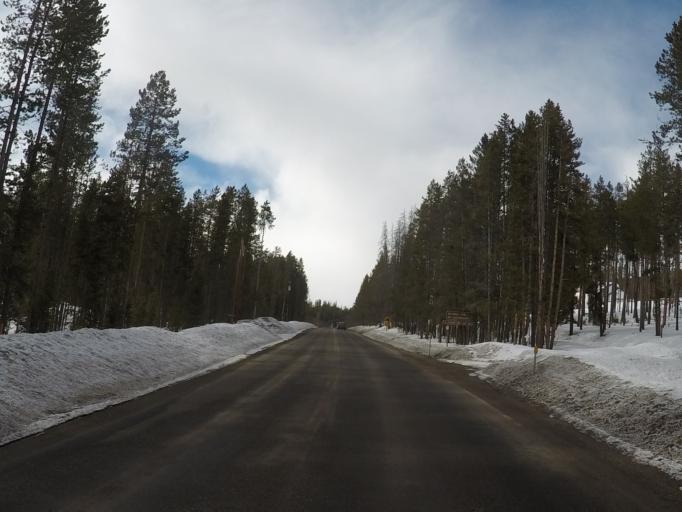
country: US
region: Montana
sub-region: Granite County
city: Philipsburg
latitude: 46.2130
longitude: -113.2762
